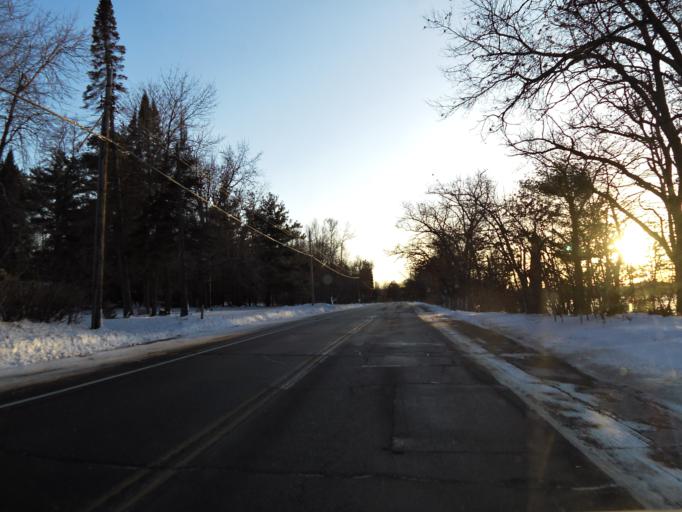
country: US
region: Minnesota
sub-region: Washington County
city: Lake Elmo
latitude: 44.9812
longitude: -92.8814
